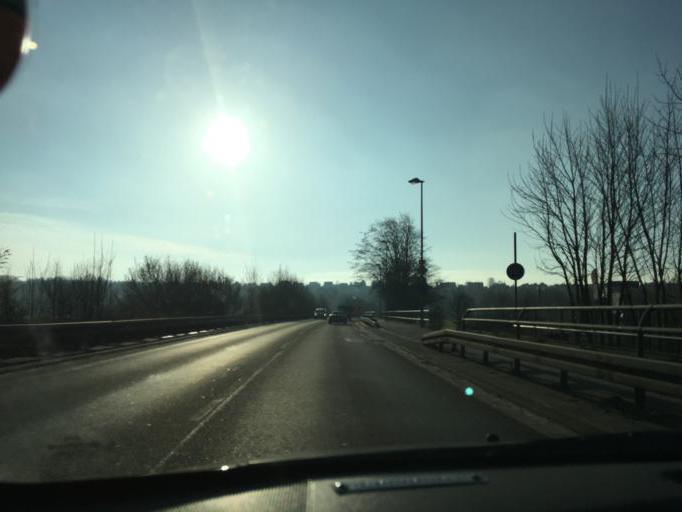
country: DE
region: North Rhine-Westphalia
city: Schwerte
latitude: 51.4395
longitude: 7.5804
